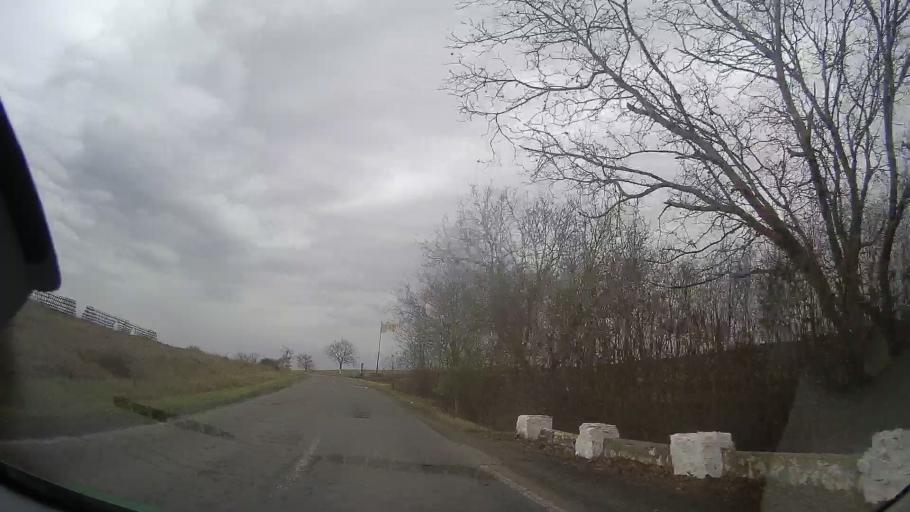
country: RO
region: Mures
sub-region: Comuna Faragau
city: Faragau
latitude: 46.7630
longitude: 24.5294
